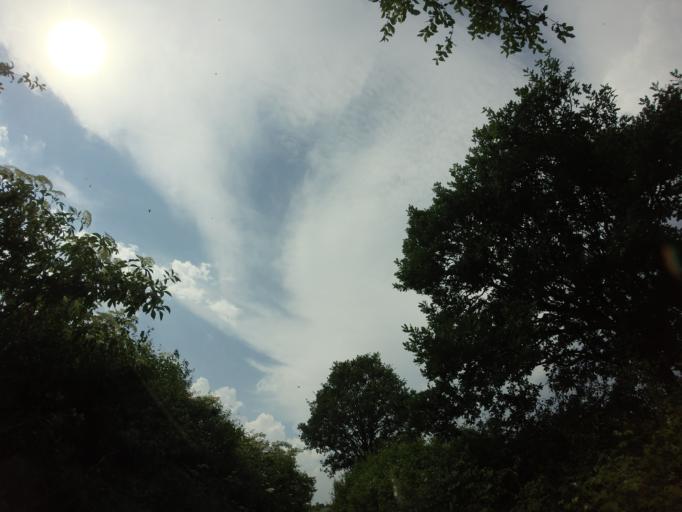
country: PL
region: West Pomeranian Voivodeship
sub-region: Powiat choszczenski
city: Krzecin
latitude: 53.1335
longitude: 15.5810
